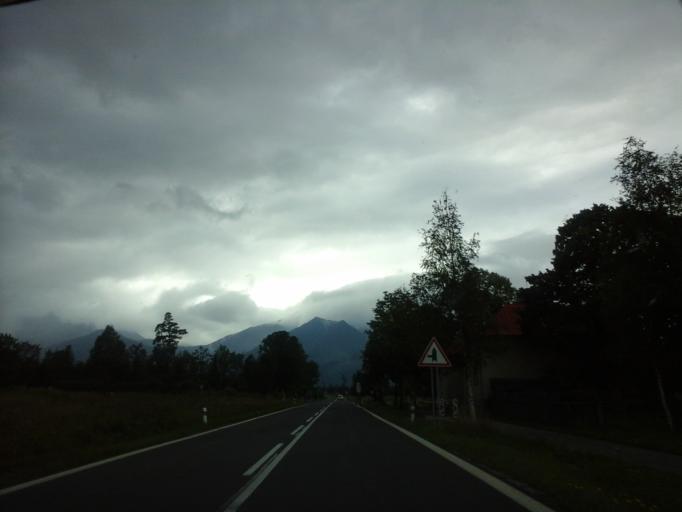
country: SK
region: Presovsky
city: Spisska Bela
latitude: 49.2102
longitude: 20.3727
